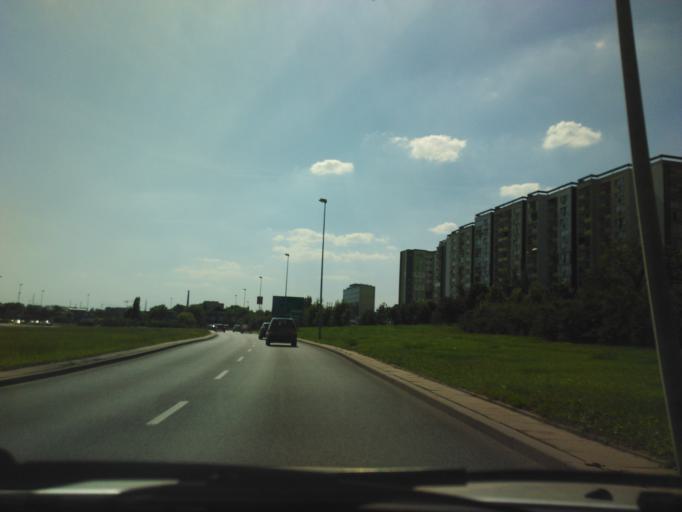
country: PL
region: West Pomeranian Voivodeship
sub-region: Powiat policki
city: Przeclaw
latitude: 53.4055
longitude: 14.5034
